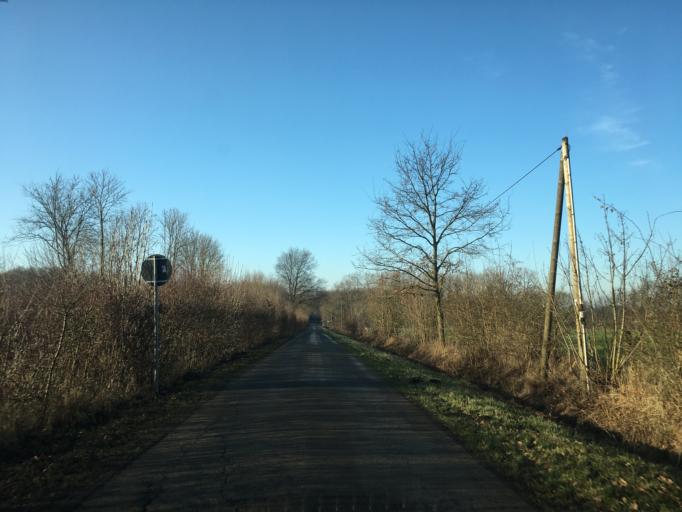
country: DE
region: North Rhine-Westphalia
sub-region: Regierungsbezirk Munster
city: Greven
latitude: 52.0244
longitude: 7.5540
